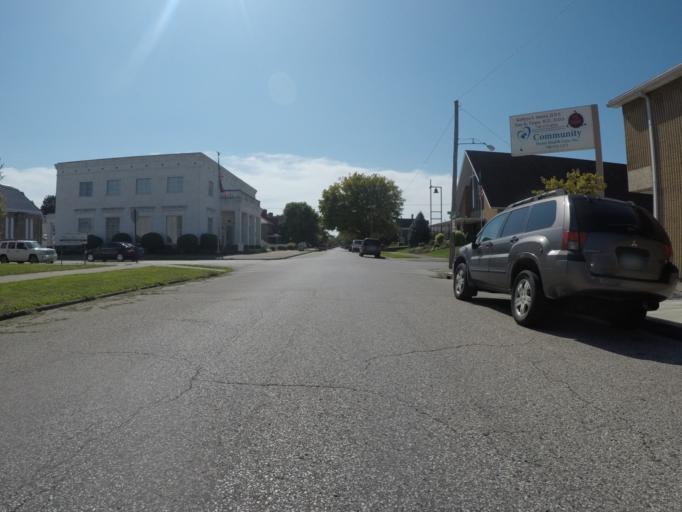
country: US
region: Ohio
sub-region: Lawrence County
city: Ironton
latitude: 38.5352
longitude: -82.6824
